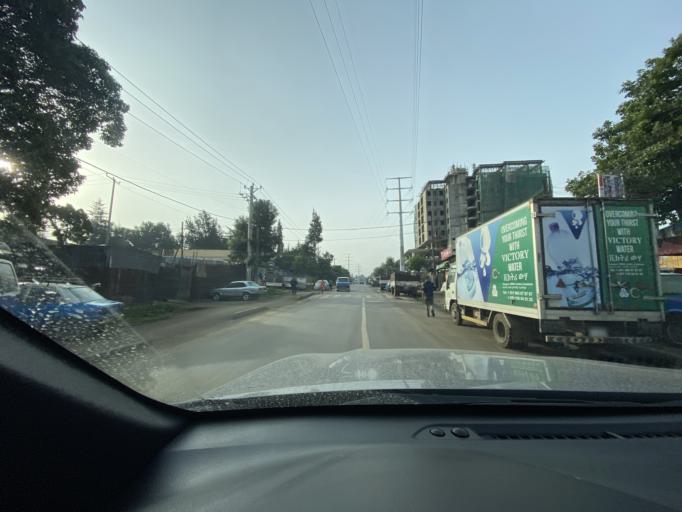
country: ET
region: Adis Abeba
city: Addis Ababa
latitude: 9.0184
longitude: 38.7272
